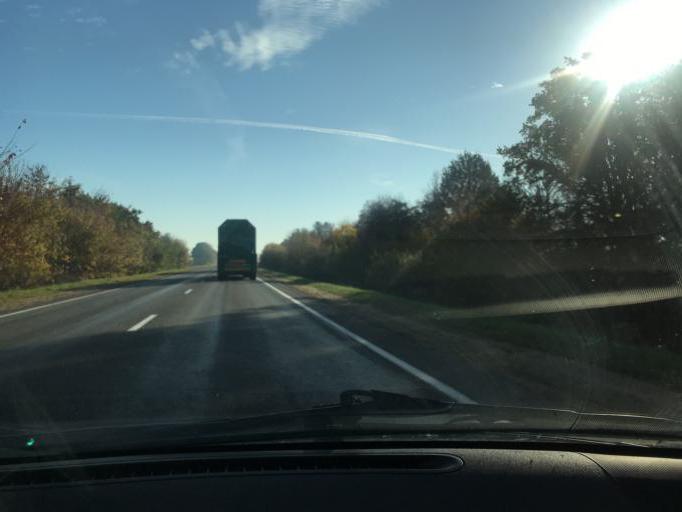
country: BY
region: Brest
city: Ivanava
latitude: 52.1492
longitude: 25.4016
